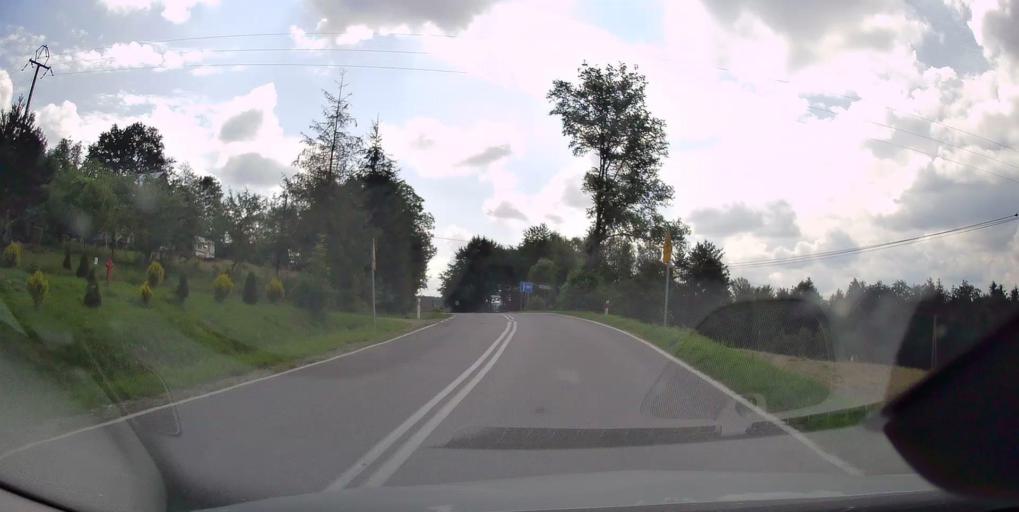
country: PL
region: Lesser Poland Voivodeship
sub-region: Powiat tarnowski
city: Zakliczyn
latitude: 49.7684
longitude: 20.7793
